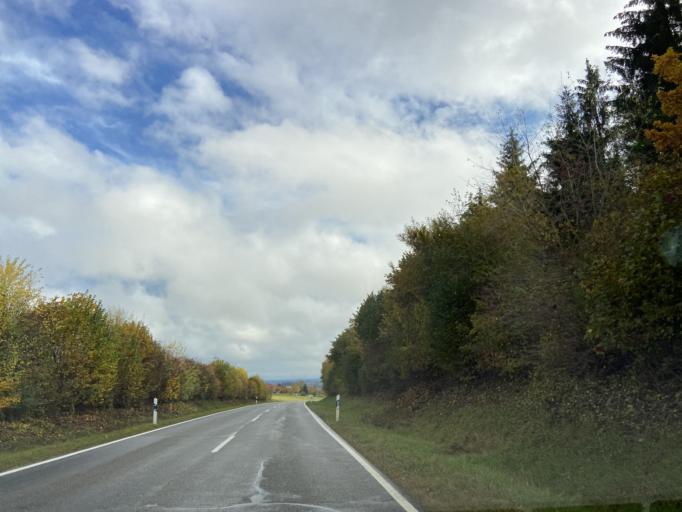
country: DE
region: Baden-Wuerttemberg
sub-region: Tuebingen Region
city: Messkirch
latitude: 48.0504
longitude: 9.0941
